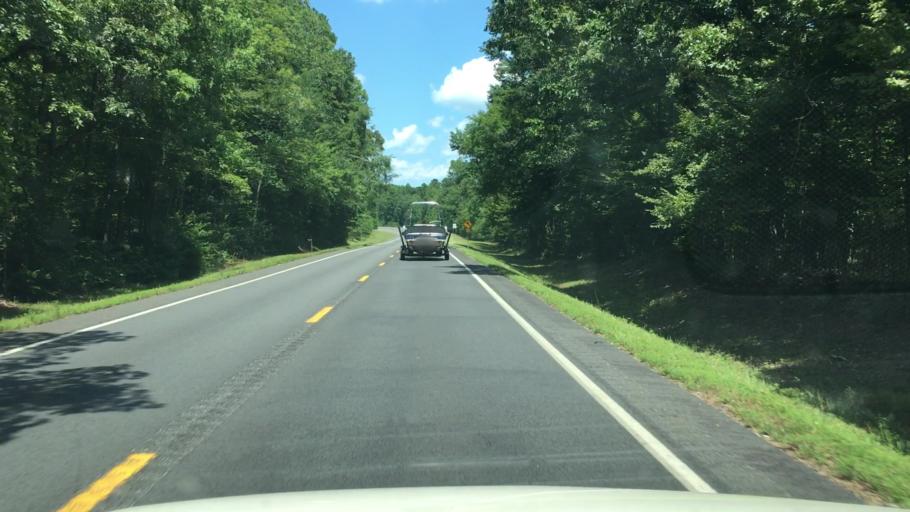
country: US
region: Arkansas
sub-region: Garland County
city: Lake Hamilton
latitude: 34.3615
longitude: -93.1679
